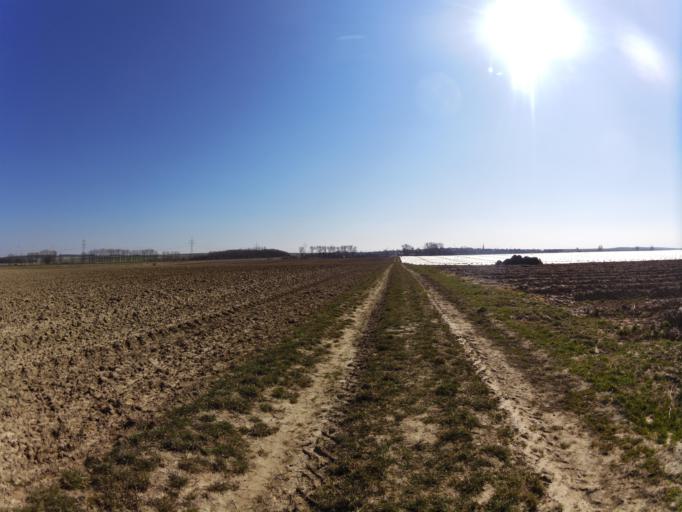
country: DE
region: Bavaria
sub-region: Regierungsbezirk Unterfranken
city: Oberpleichfeld
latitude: 49.8897
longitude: 10.0799
